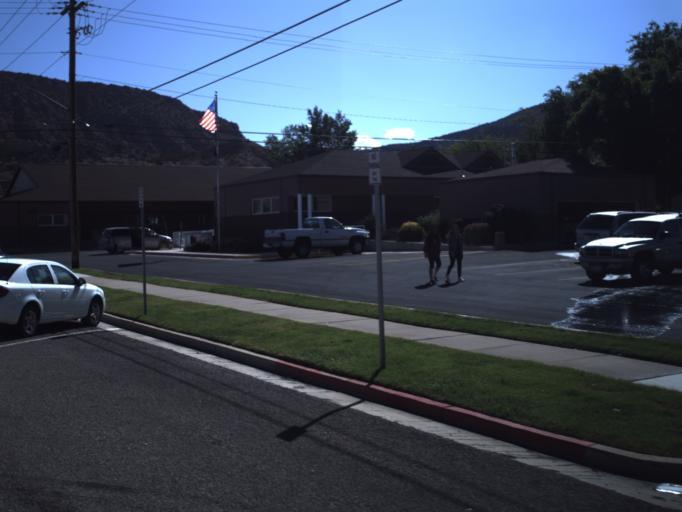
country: US
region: Utah
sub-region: Iron County
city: Cedar City
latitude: 37.6809
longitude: -113.0597
